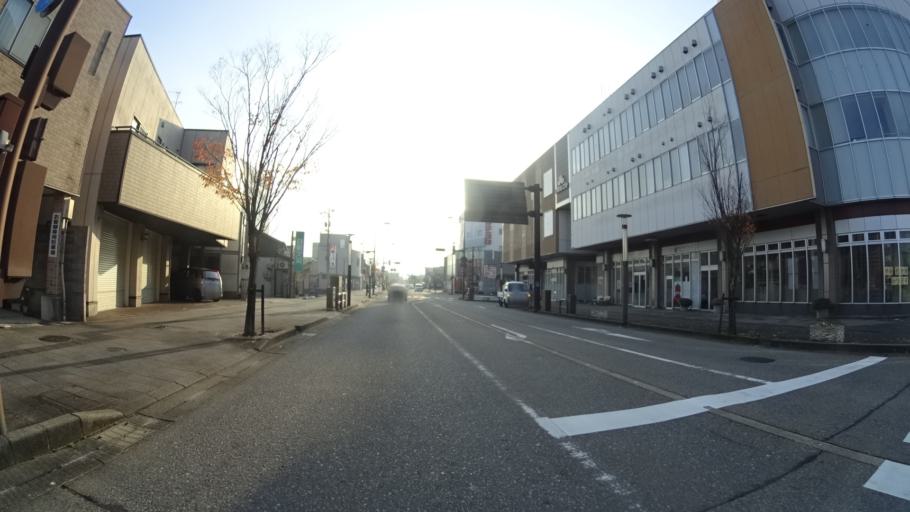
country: JP
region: Ishikawa
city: Nanao
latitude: 37.0438
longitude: 136.9642
